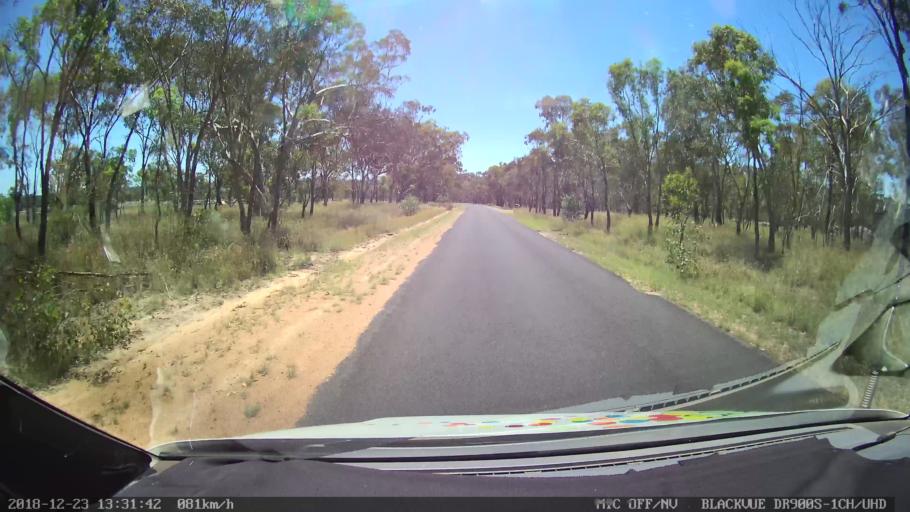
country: AU
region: New South Wales
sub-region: Armidale Dumaresq
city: Armidale
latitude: -30.4634
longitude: 151.3017
